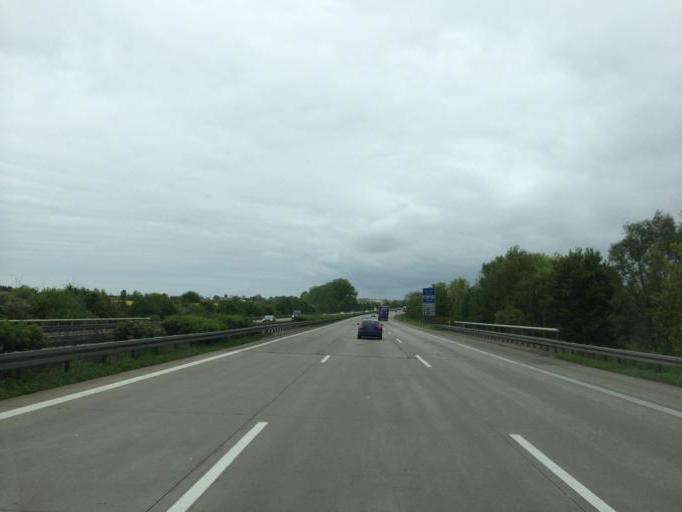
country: DE
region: Saxony-Anhalt
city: Gross Santersleben
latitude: 52.1883
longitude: 11.4268
